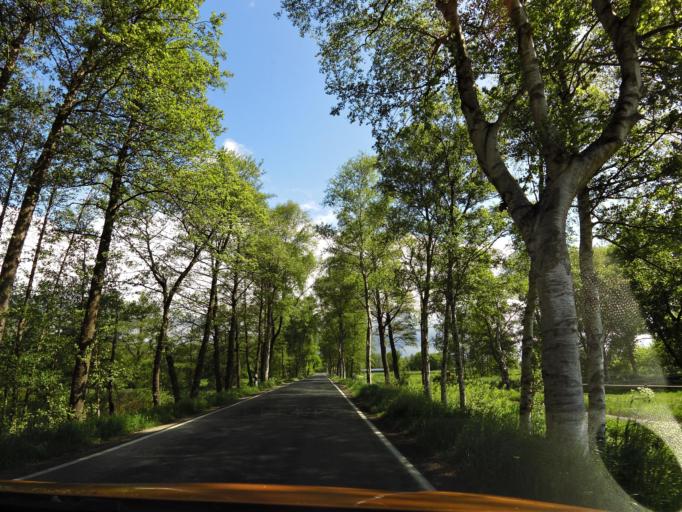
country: DE
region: Lower Saxony
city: Hatten
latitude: 53.1482
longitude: 8.3683
